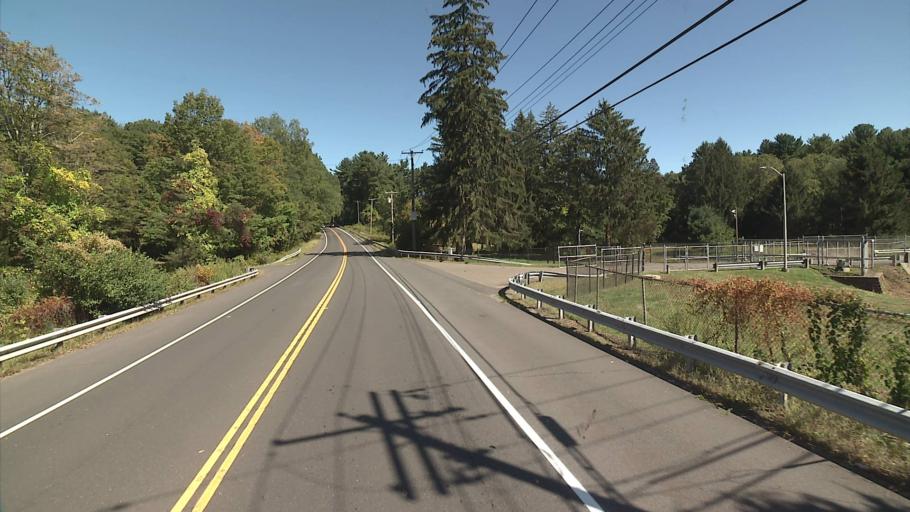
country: US
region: Connecticut
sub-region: New Haven County
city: Woodbridge
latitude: 41.3775
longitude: -72.9765
